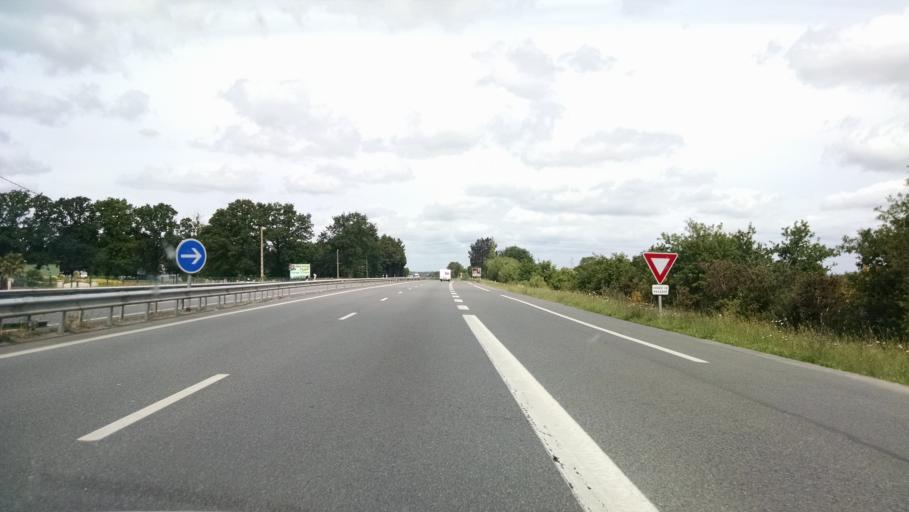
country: FR
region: Pays de la Loire
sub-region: Departement de la Loire-Atlantique
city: Pontchateau
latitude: 47.4253
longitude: -2.0578
